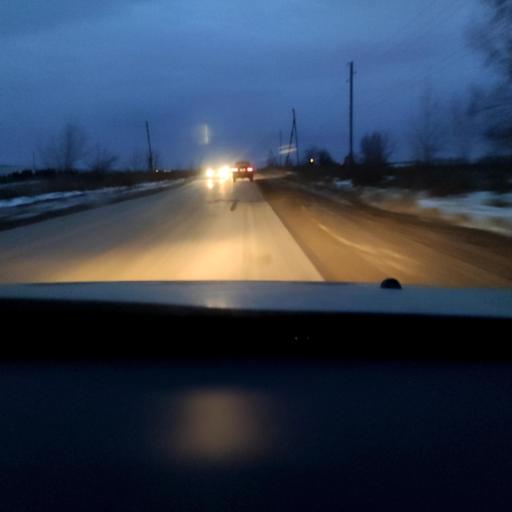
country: RU
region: Perm
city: Gamovo
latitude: 57.8763
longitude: 56.1018
